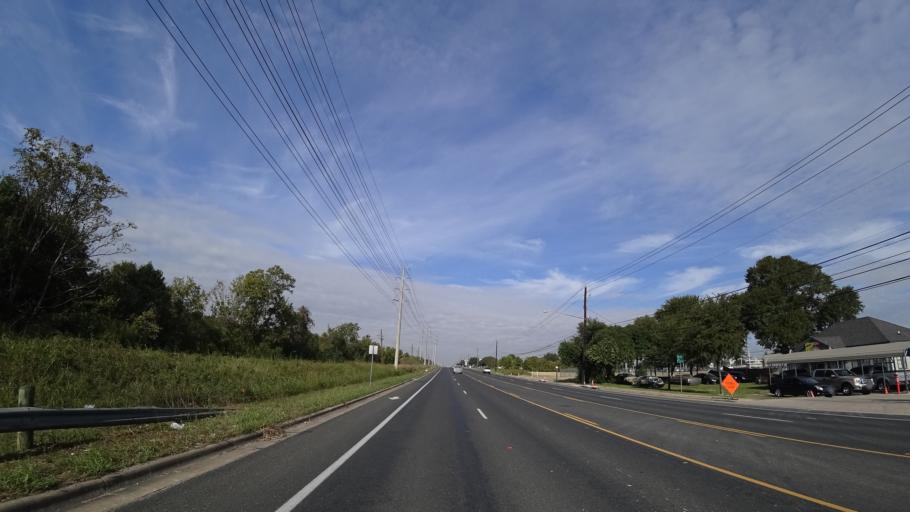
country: US
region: Texas
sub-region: Travis County
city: Austin
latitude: 30.2085
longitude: -97.7229
